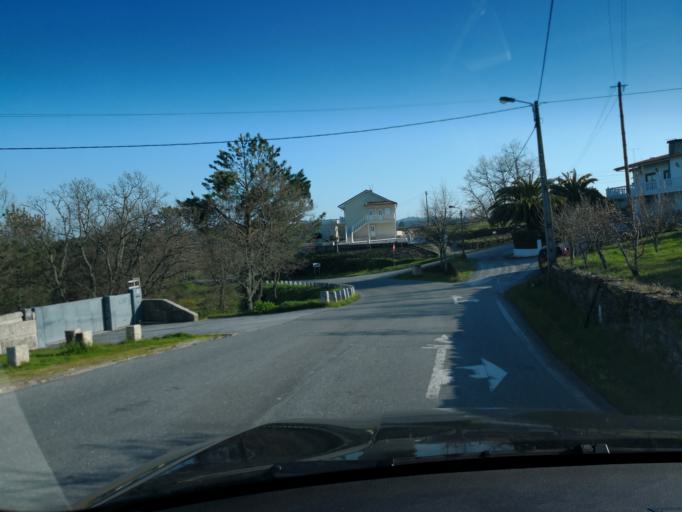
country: PT
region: Vila Real
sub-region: Sabrosa
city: Sabrosa
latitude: 41.3559
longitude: -7.6133
